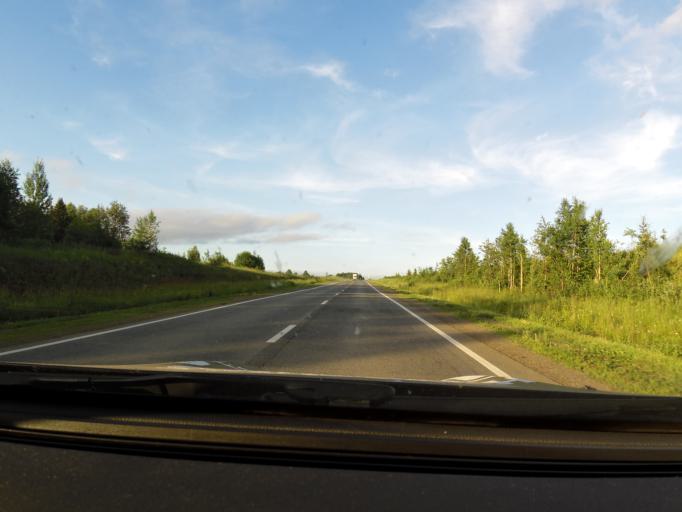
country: RU
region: Perm
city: Siva
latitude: 58.4878
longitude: 54.0994
